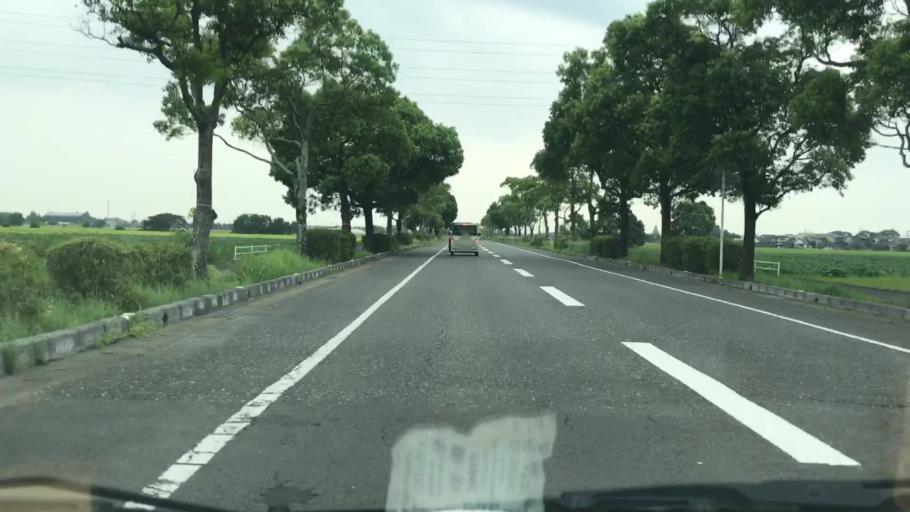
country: JP
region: Saga Prefecture
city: Saga-shi
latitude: 33.2317
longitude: 130.3060
